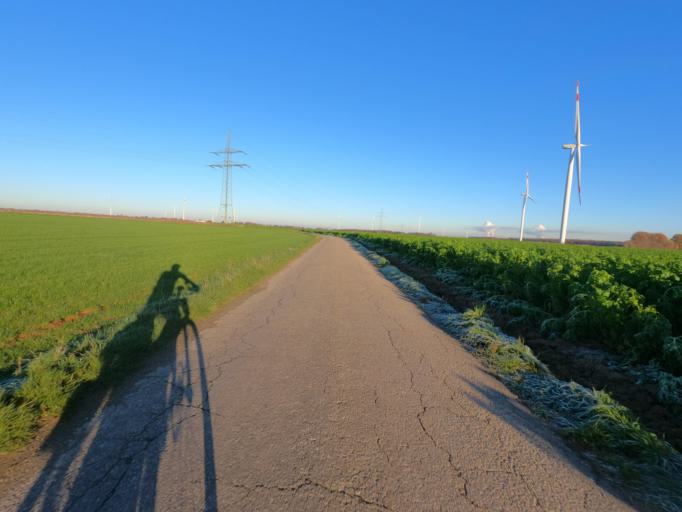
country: DE
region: North Rhine-Westphalia
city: Geilenkirchen
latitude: 50.9994
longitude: 6.0881
